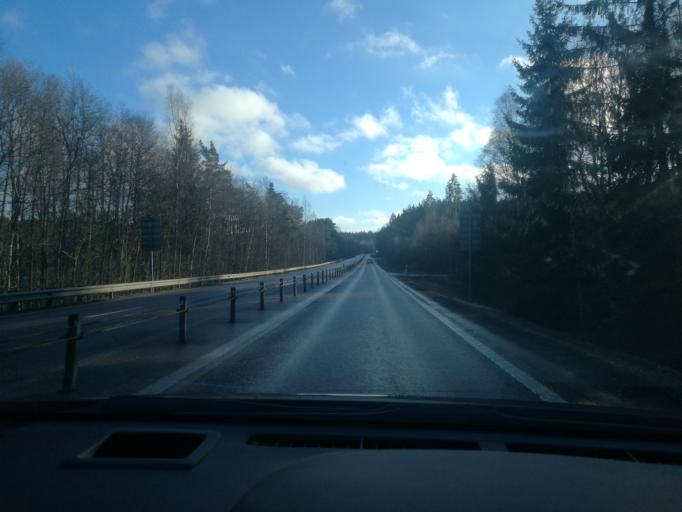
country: SE
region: OEstergoetland
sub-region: Norrkopings Kommun
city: Jursla
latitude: 58.7577
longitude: 16.1742
